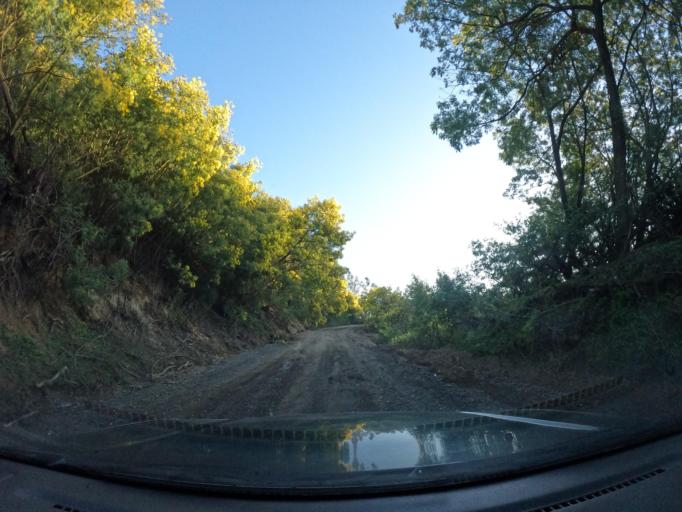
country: CL
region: Biobio
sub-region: Provincia de Concepcion
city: Chiguayante
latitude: -37.0174
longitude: -72.8541
